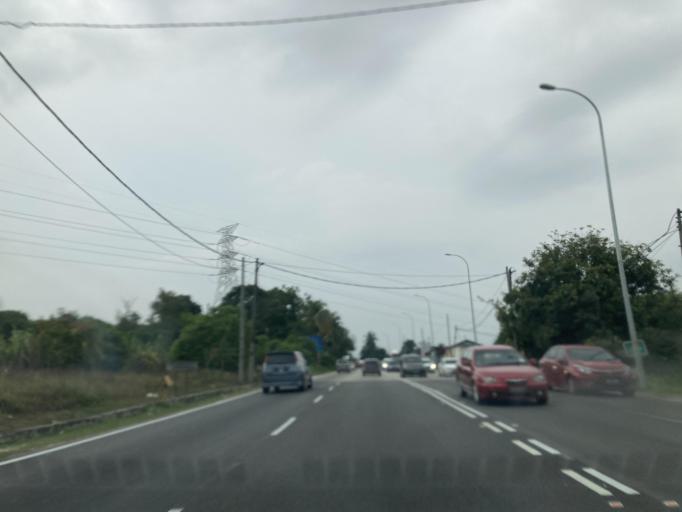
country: MY
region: Selangor
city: Kuang
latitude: 3.2186
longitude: 101.5281
